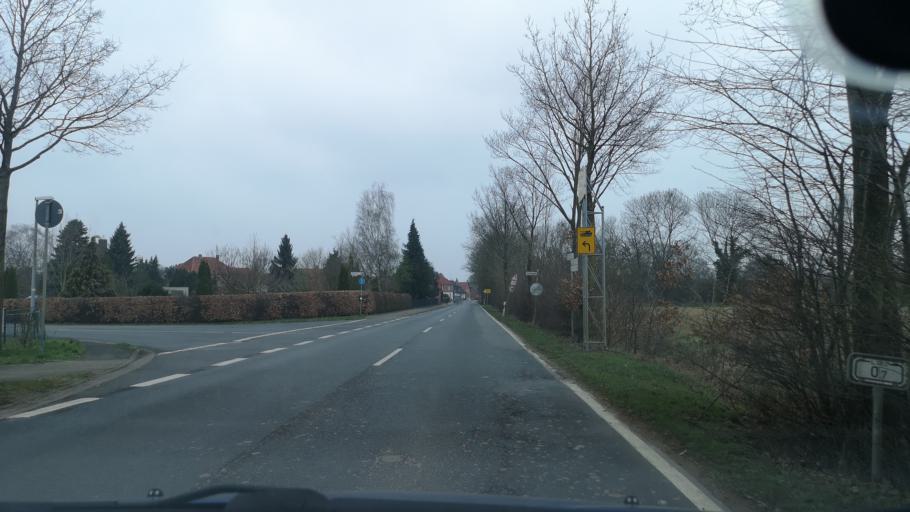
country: DE
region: Lower Saxony
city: Schwarmstedt
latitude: 52.5950
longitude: 9.5700
